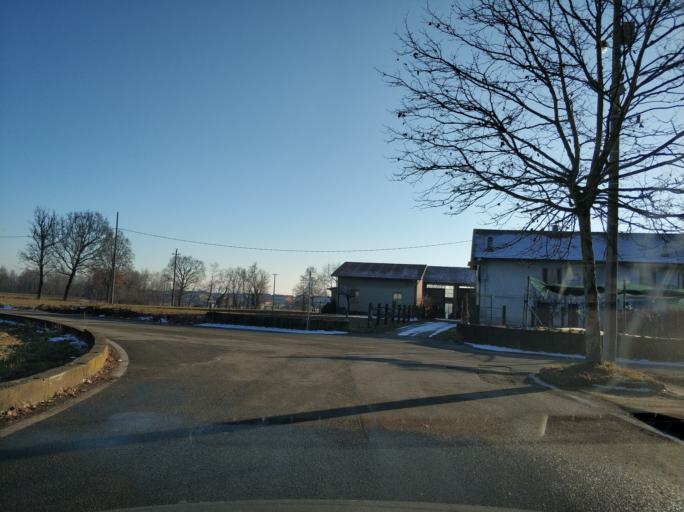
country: IT
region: Piedmont
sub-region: Provincia di Torino
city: San Francesco al Campo
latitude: 45.2323
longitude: 7.6596
